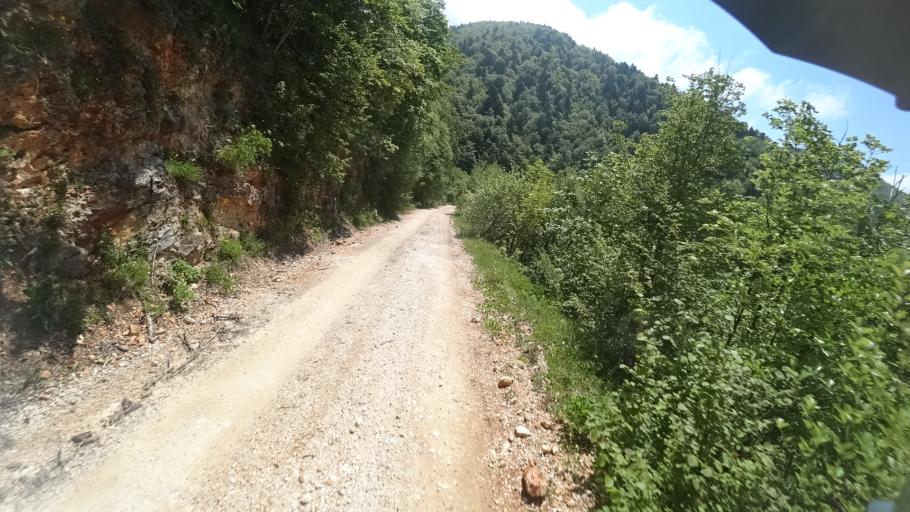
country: BA
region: Federation of Bosnia and Herzegovina
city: Orasac
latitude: 44.5767
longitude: 15.8584
